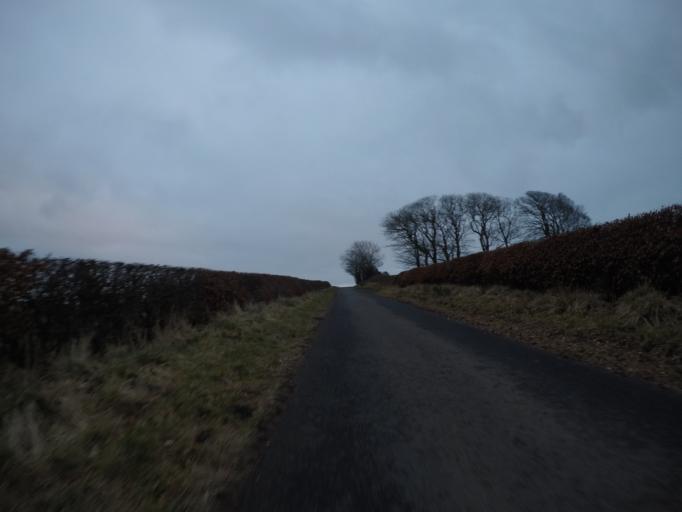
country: GB
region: Scotland
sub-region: North Ayrshire
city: Dalry
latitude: 55.6855
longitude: -4.7337
